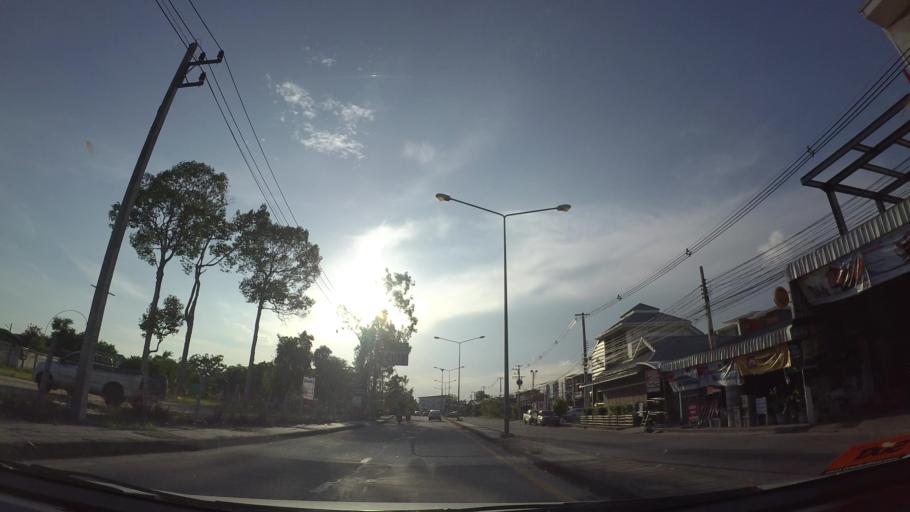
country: TH
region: Rayong
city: Rayong
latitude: 12.6837
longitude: 101.2868
